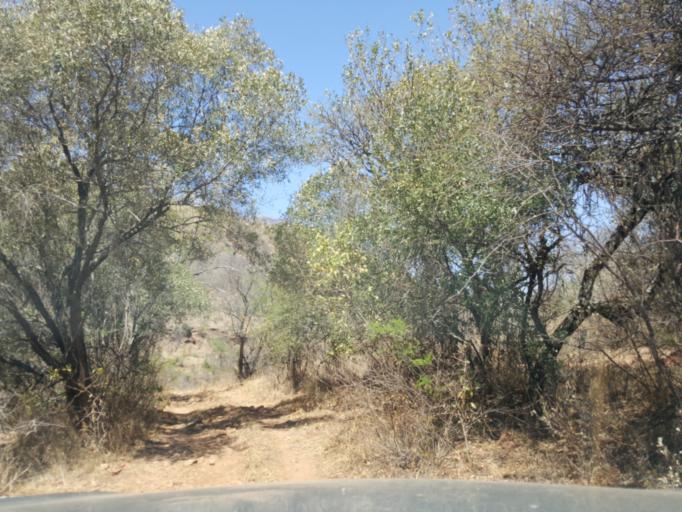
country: BW
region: South East
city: Lobatse
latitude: -25.1485
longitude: 25.6701
